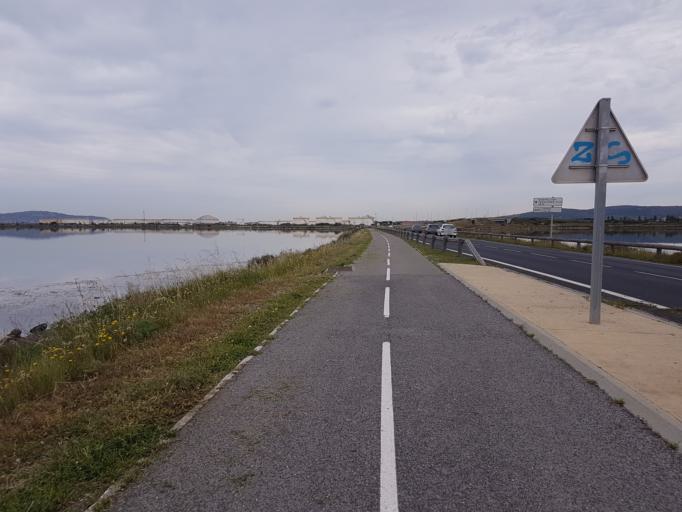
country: FR
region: Languedoc-Roussillon
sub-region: Departement de l'Herault
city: Frontignan
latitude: 43.4356
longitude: 3.7689
